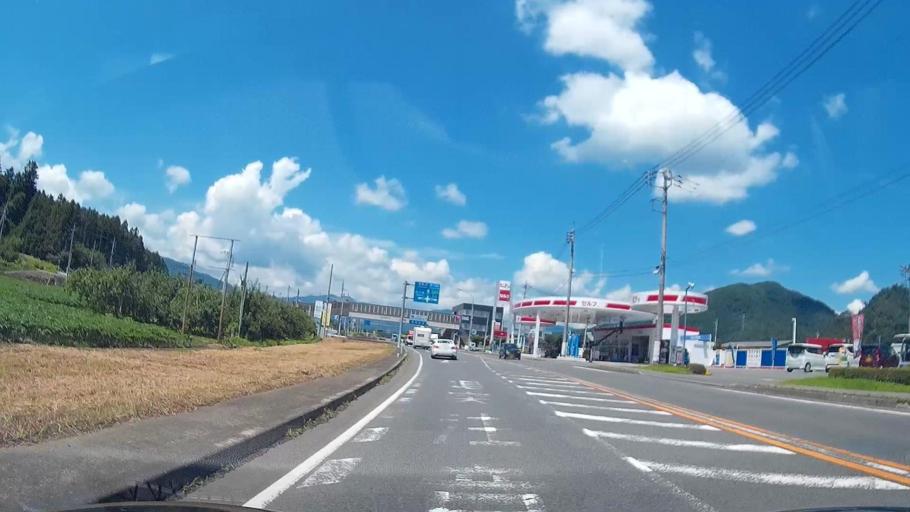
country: JP
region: Gunma
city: Numata
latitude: 36.6768
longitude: 138.9790
